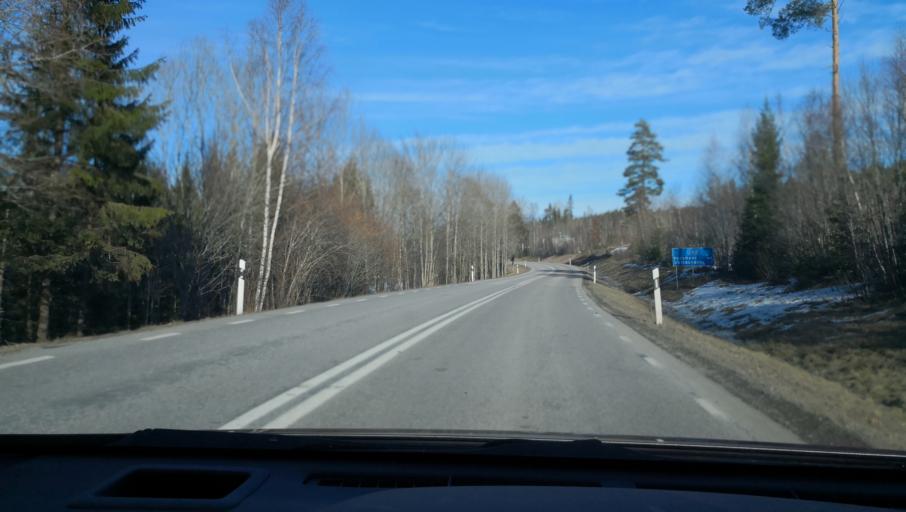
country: SE
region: Uppsala
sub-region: Uppsala Kommun
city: Vattholma
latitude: 60.0744
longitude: 17.7593
